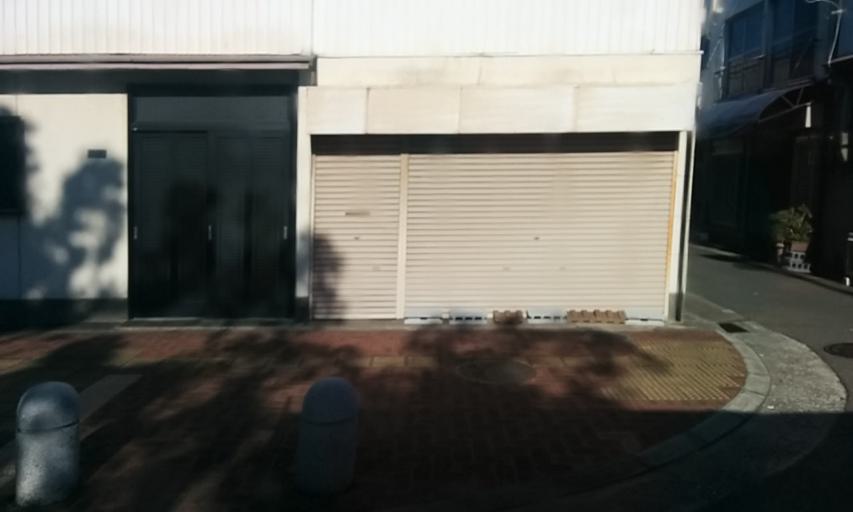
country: JP
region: Wakayama
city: Wakayama-shi
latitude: 34.2368
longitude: 135.1685
